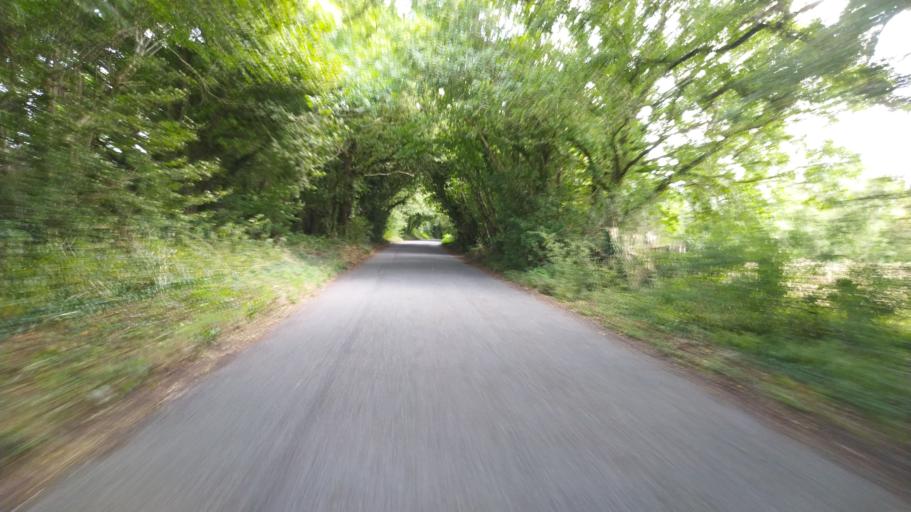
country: GB
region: England
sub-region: Dorset
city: Blandford Forum
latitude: 50.8314
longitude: -2.1199
